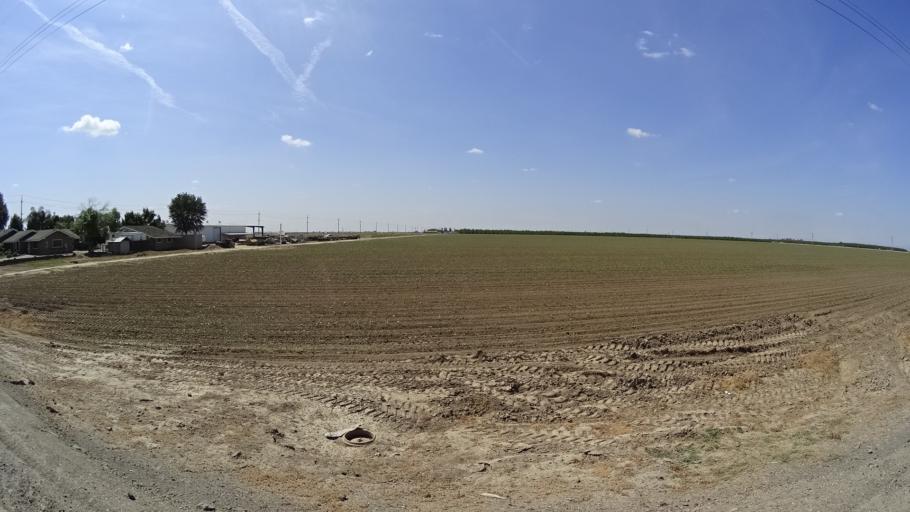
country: US
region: California
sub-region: Kings County
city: Home Garden
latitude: 36.2694
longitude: -119.5846
